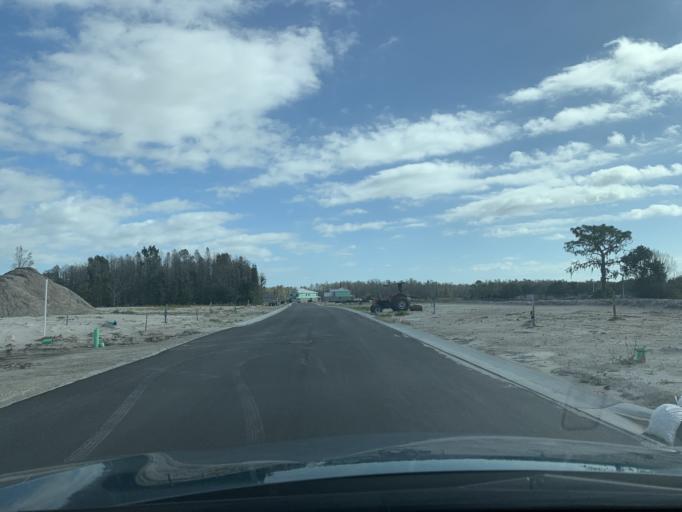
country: US
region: Florida
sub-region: Pasco County
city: Trinity
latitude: 28.1980
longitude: -82.6736
